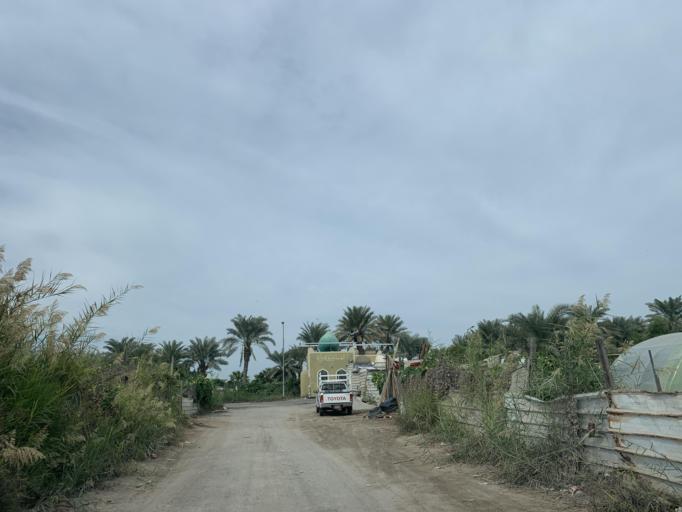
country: BH
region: Central Governorate
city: Madinat Hamad
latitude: 26.1130
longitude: 50.4762
